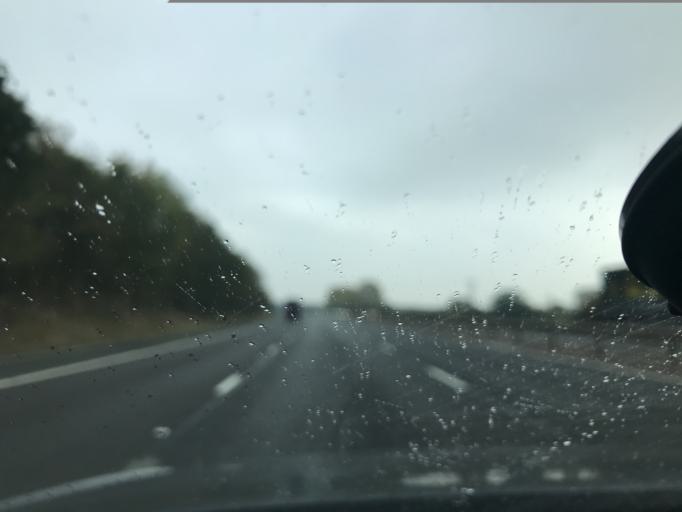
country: GB
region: England
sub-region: Oxfordshire
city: Wheatley
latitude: 51.7488
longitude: -1.1034
